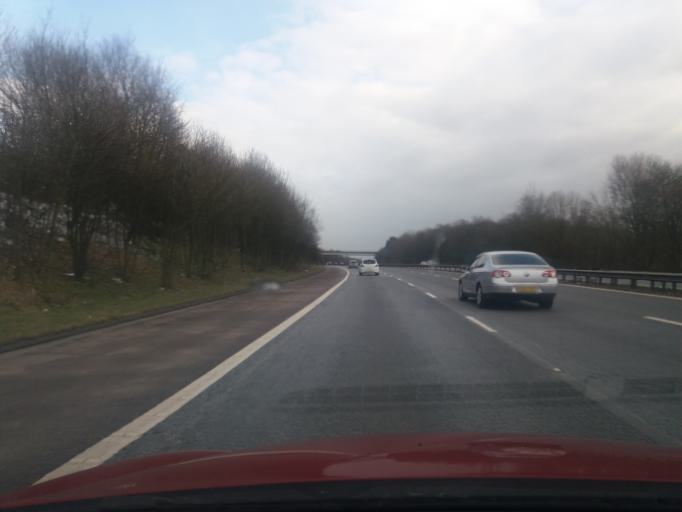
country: GB
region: England
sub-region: Lancashire
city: Clayton-le-Woods
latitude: 53.6976
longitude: -2.6298
